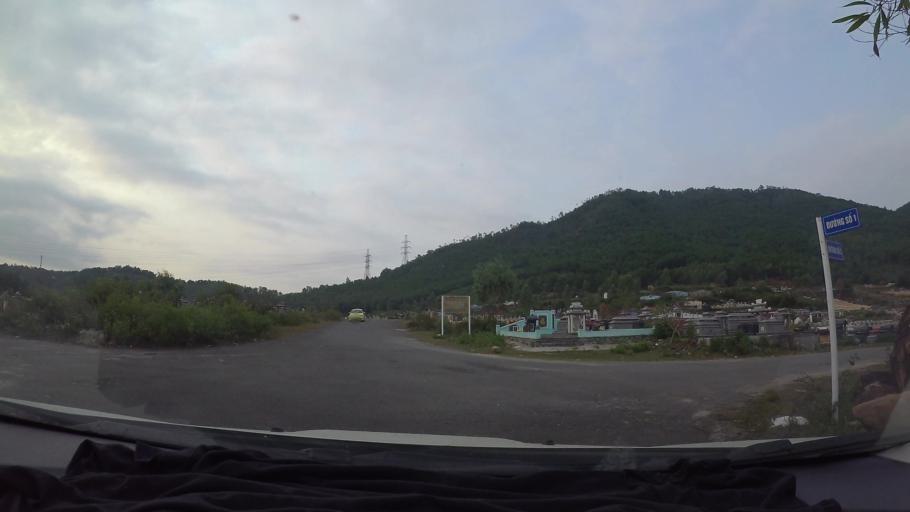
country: VN
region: Da Nang
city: Lien Chieu
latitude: 16.0609
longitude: 108.1121
